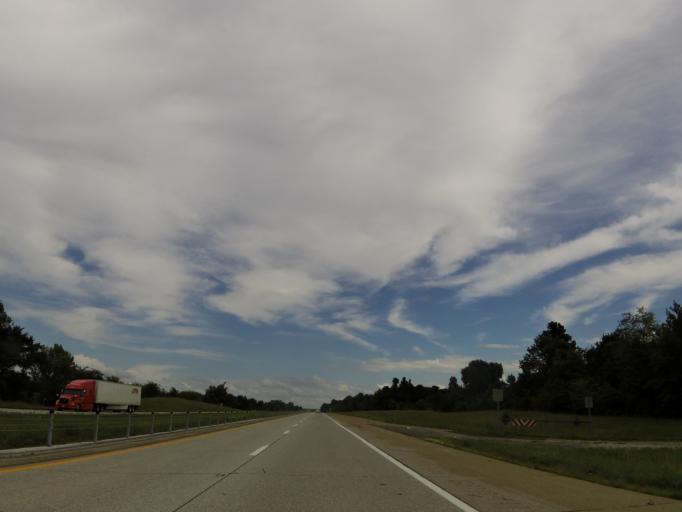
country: US
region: Kentucky
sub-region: Trigg County
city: Cadiz
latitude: 36.9756
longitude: -87.8985
